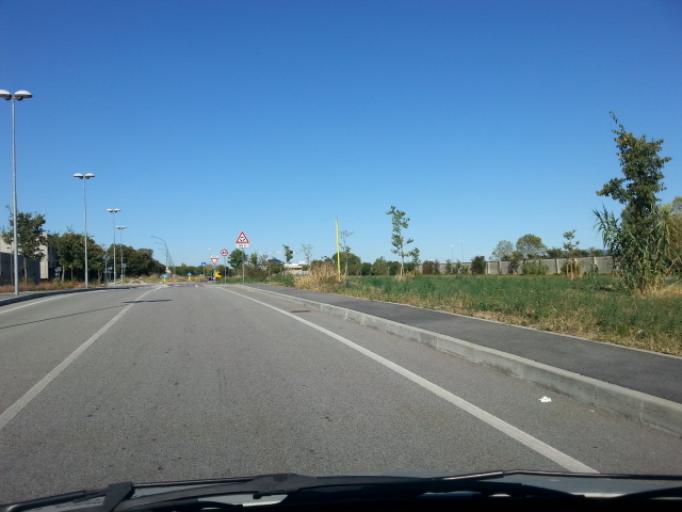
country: IT
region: Piedmont
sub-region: Provincia di Torino
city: Fornaci
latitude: 45.0371
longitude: 7.5894
